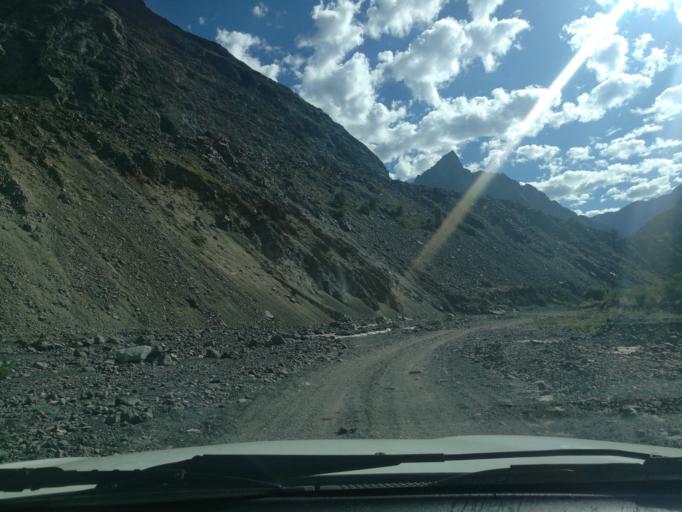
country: CL
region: O'Higgins
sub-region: Provincia de Cachapoal
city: Machali
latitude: -34.3648
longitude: -70.3190
